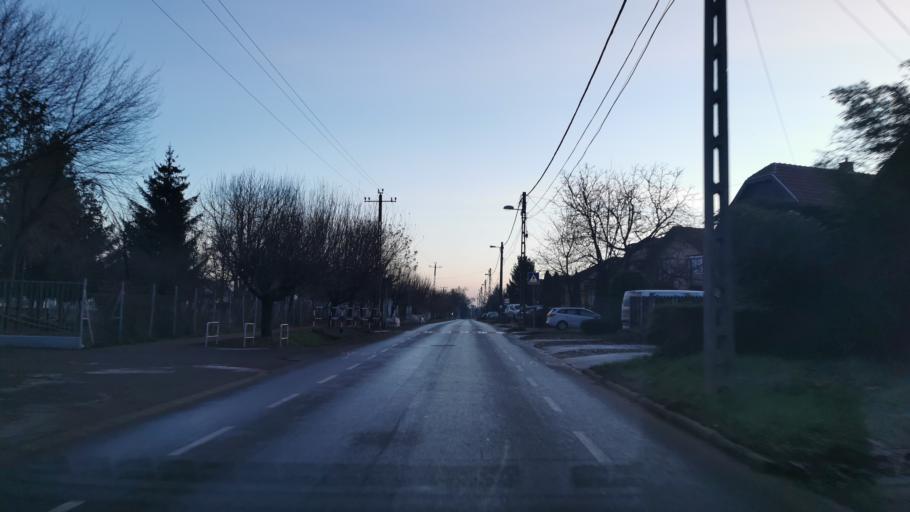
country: HU
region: Hajdu-Bihar
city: Hajduboszormeny
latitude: 47.5976
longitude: 21.5714
